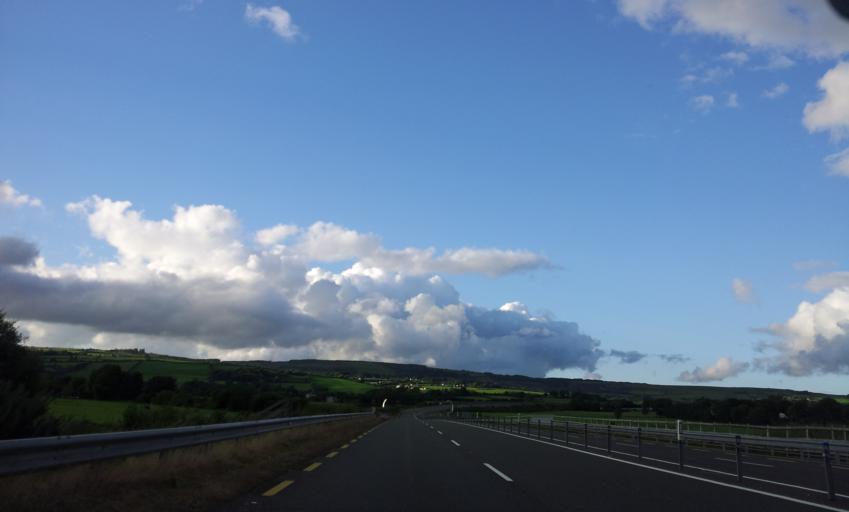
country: IE
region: Munster
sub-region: Ciarrai
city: Castleisland
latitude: 52.2380
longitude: -9.4860
